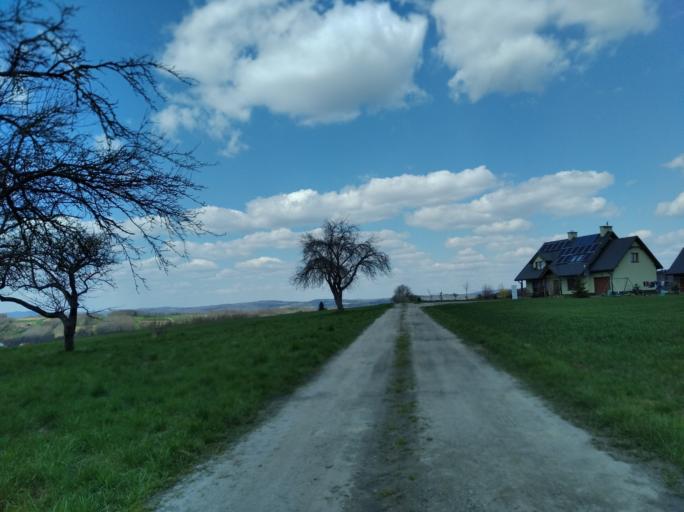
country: PL
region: Subcarpathian Voivodeship
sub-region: Powiat strzyzowski
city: Wysoka Strzyzowska
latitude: 49.8461
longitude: 21.7681
